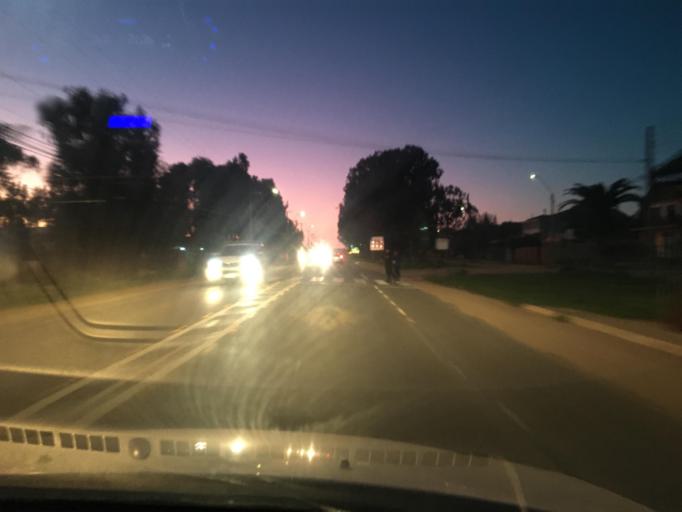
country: CL
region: Valparaiso
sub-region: San Antonio Province
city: El Tabo
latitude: -33.4280
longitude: -71.6901
